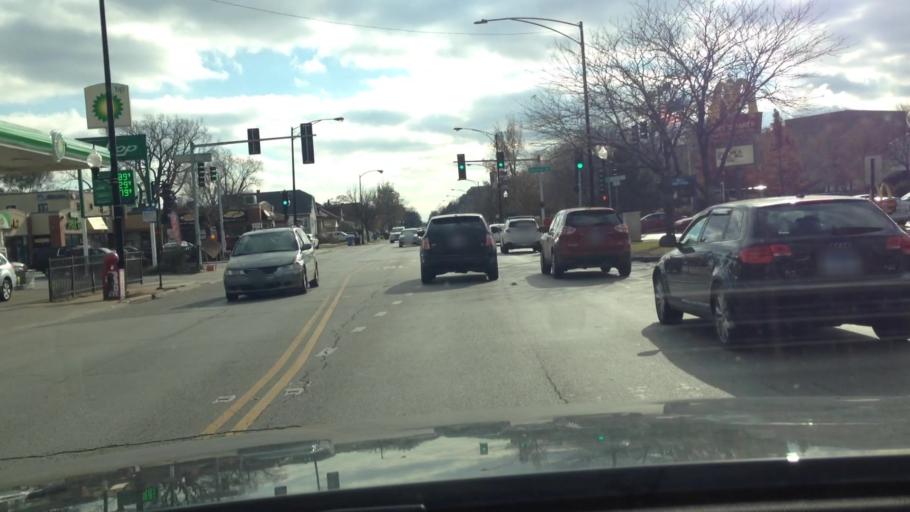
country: US
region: Illinois
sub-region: Cook County
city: Harwood Heights
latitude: 41.9608
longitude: -87.7868
